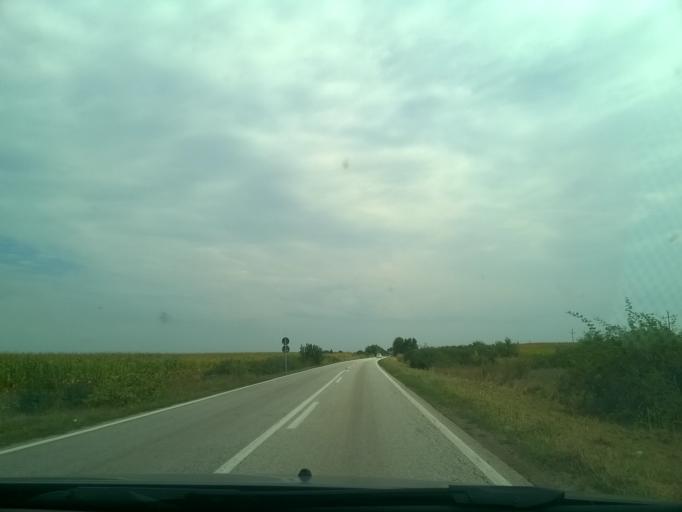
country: RS
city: Sutjeska
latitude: 45.3784
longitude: 20.6783
